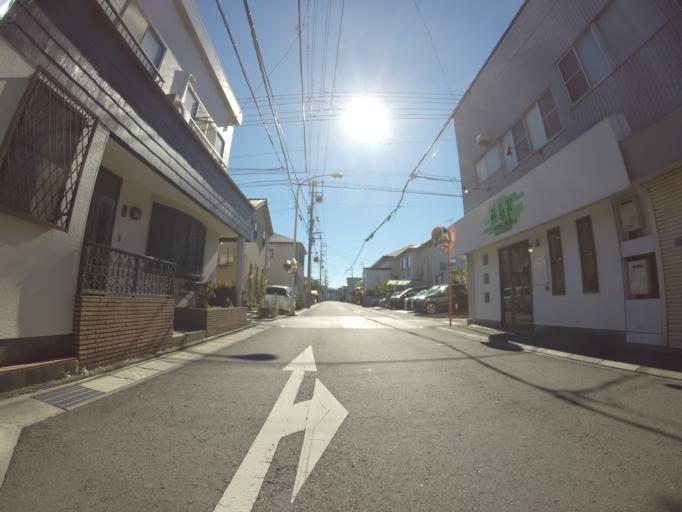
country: JP
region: Shizuoka
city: Shizuoka-shi
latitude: 34.9898
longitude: 138.3885
